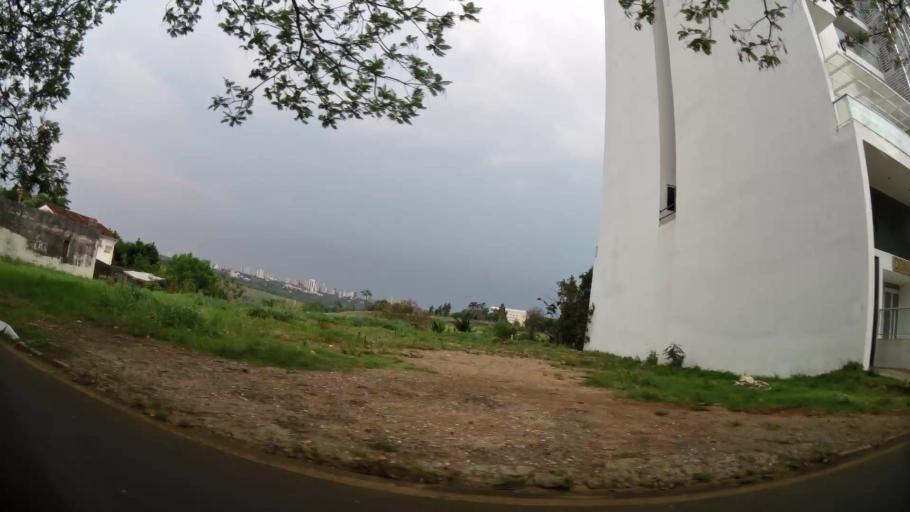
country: PY
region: Alto Parana
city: Ciudad del Este
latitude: -25.5182
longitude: -54.6069
